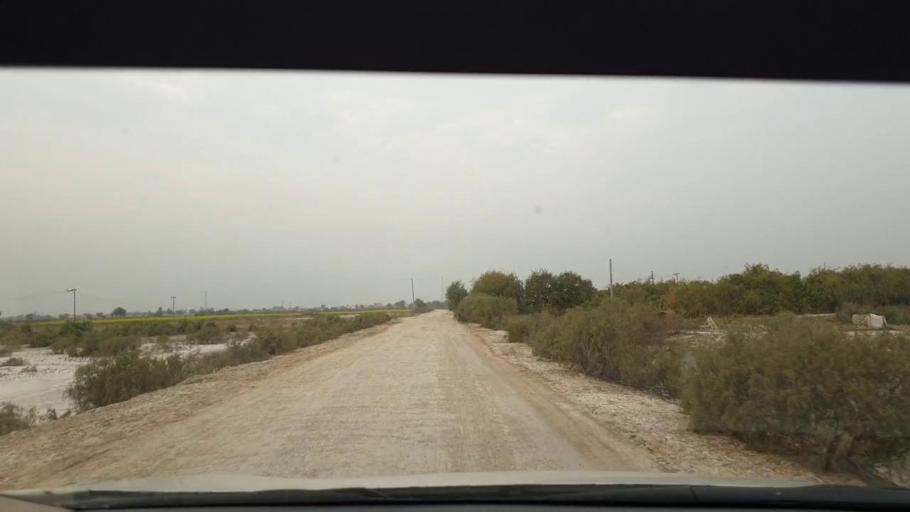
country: PK
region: Sindh
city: Sinjhoro
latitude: 25.9256
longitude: 68.7547
